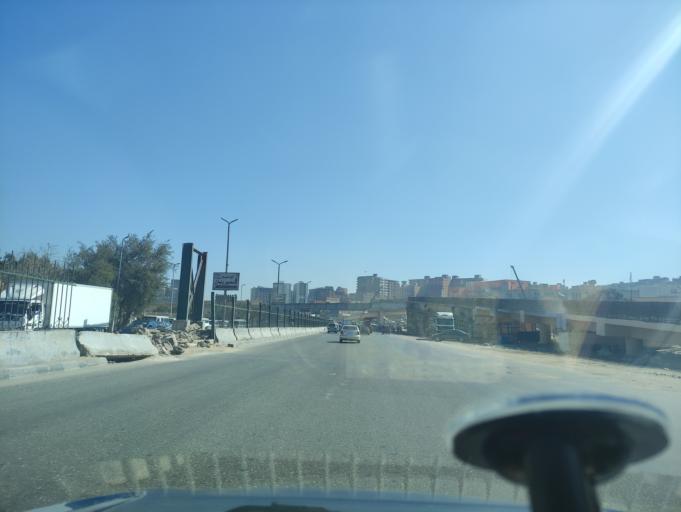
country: EG
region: Muhafazat al Qahirah
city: Cairo
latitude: 30.0482
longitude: 31.2841
